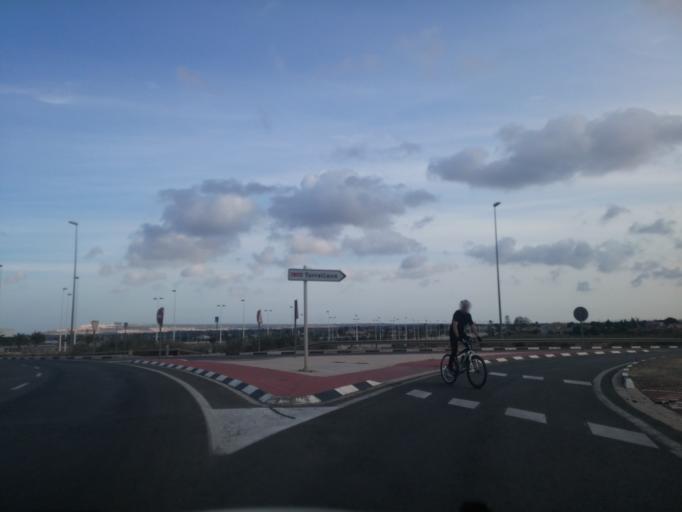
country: ES
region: Valencia
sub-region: Provincia de Alicante
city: Santa Pola
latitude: 38.2976
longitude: -0.5787
